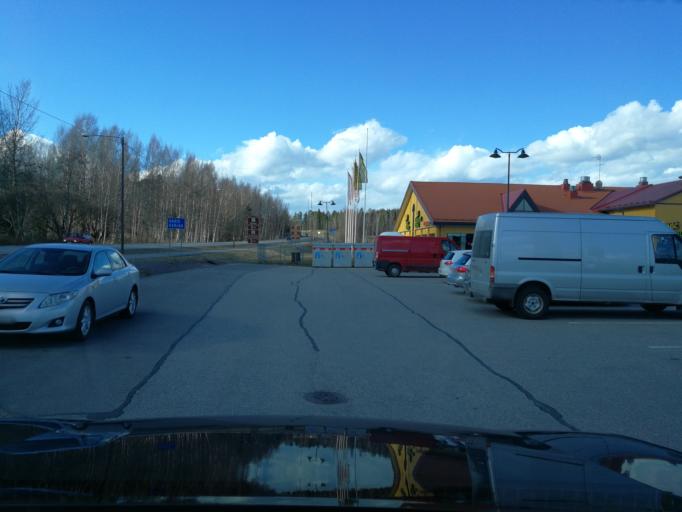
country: FI
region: Uusimaa
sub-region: Raaseporin
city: Karis
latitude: 60.0542
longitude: 23.6467
